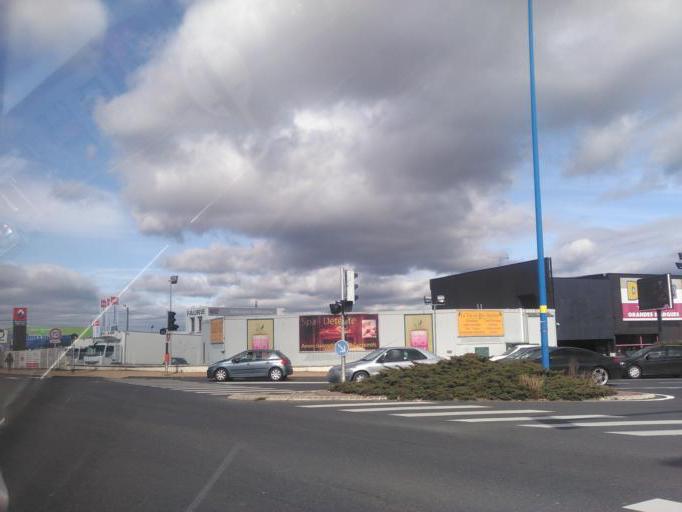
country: FR
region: Auvergne
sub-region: Departement du Puy-de-Dome
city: Perignat-les-Sarlieve
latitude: 45.7524
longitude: 3.1318
